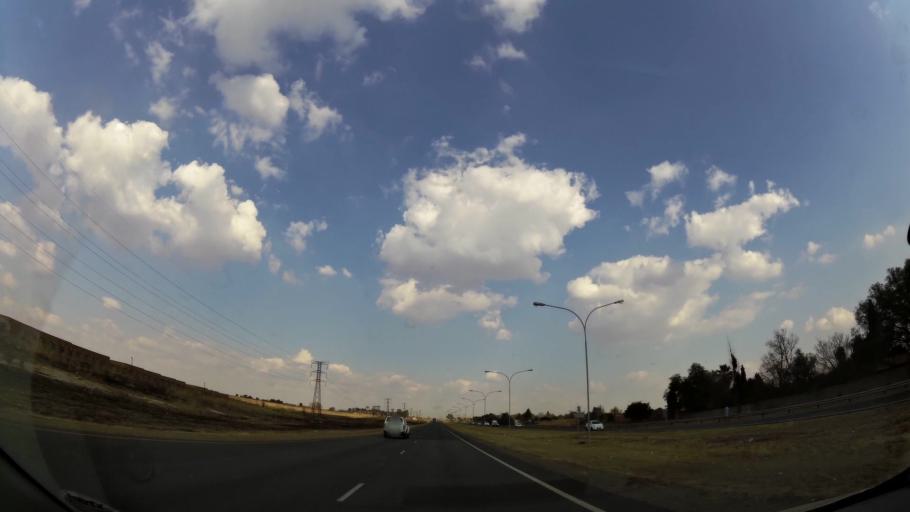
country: ZA
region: Gauteng
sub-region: Ekurhuleni Metropolitan Municipality
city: Brakpan
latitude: -26.2652
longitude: 28.3247
